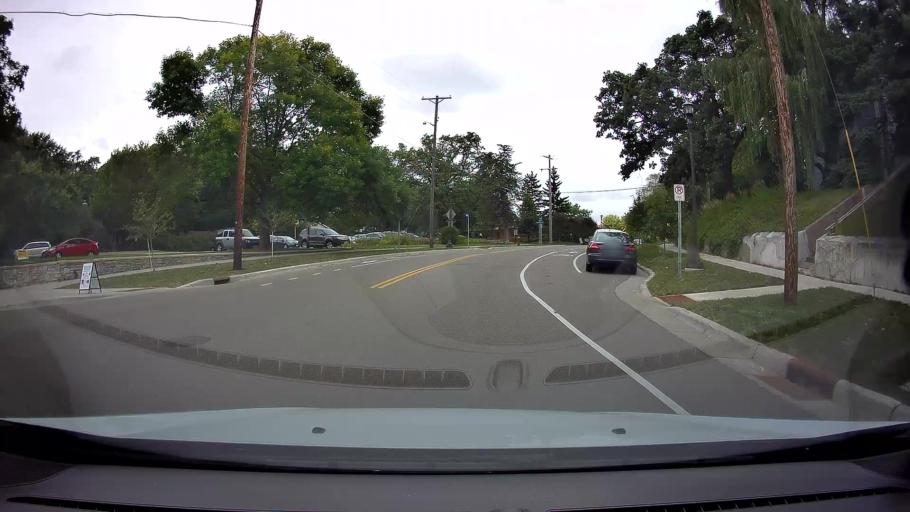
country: US
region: Minnesota
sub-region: Ramsey County
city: Lauderdale
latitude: 44.9797
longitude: -93.1932
